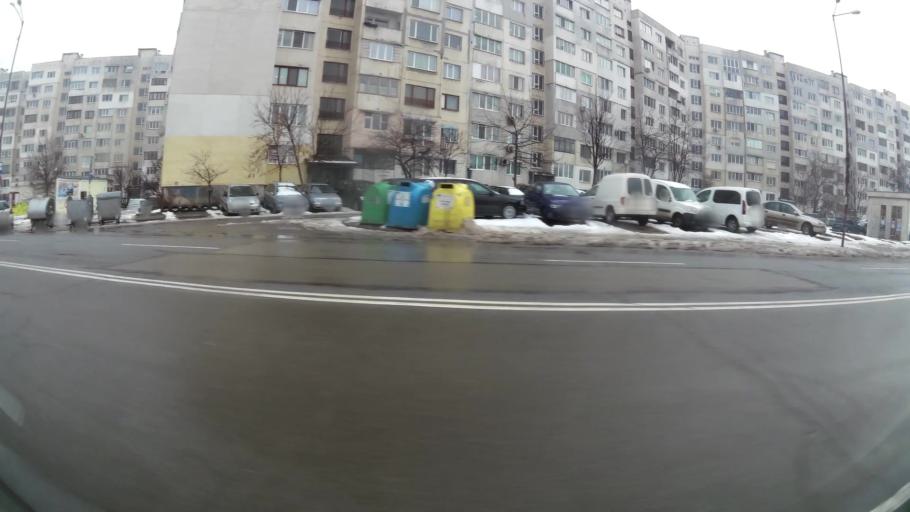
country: BG
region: Sofia-Capital
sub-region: Stolichna Obshtina
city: Sofia
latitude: 42.6899
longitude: 23.2592
